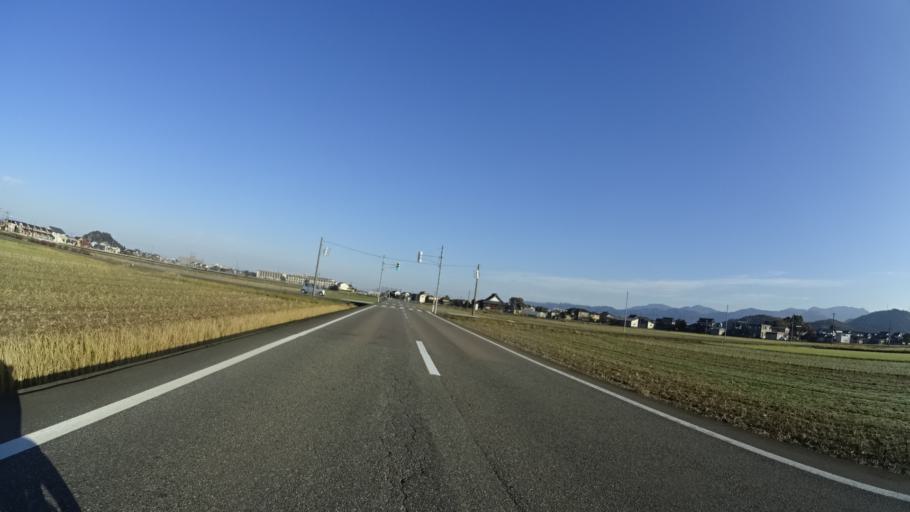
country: JP
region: Fukui
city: Fukui-shi
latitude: 36.0667
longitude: 136.2567
